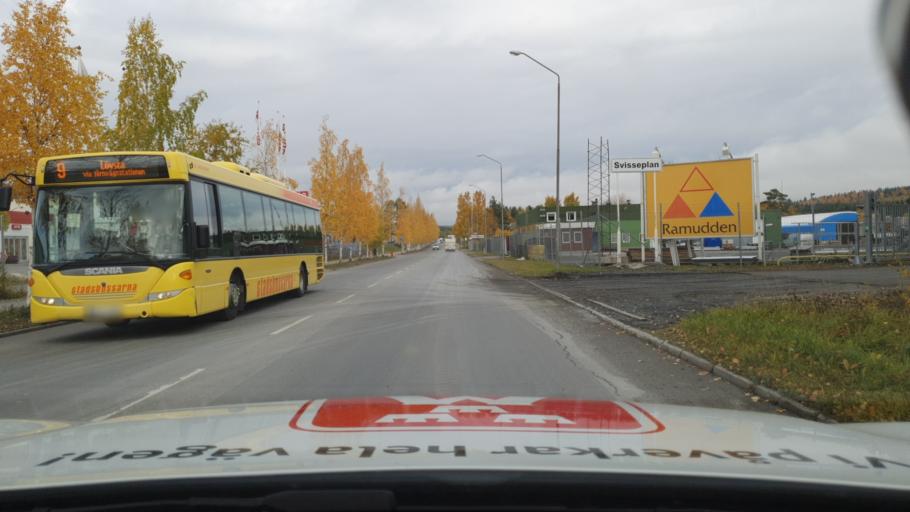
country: SE
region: Jaemtland
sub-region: OEstersunds Kommun
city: Ostersund
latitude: 63.1654
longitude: 14.6892
